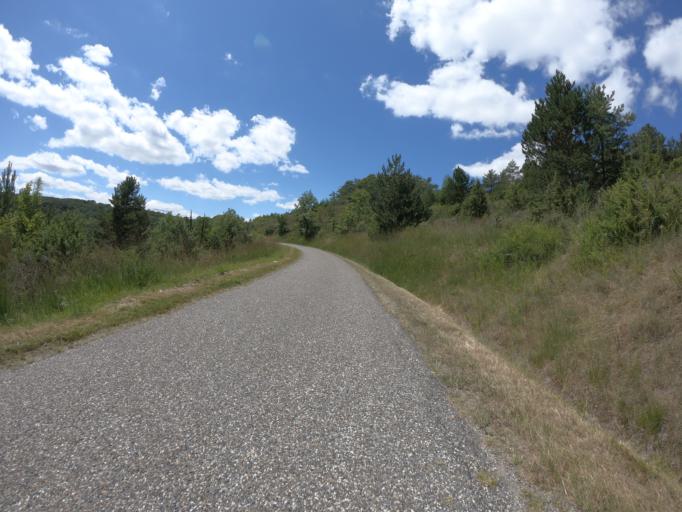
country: FR
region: Midi-Pyrenees
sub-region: Departement de l'Ariege
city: Mirepoix
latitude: 43.0569
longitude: 1.8434
